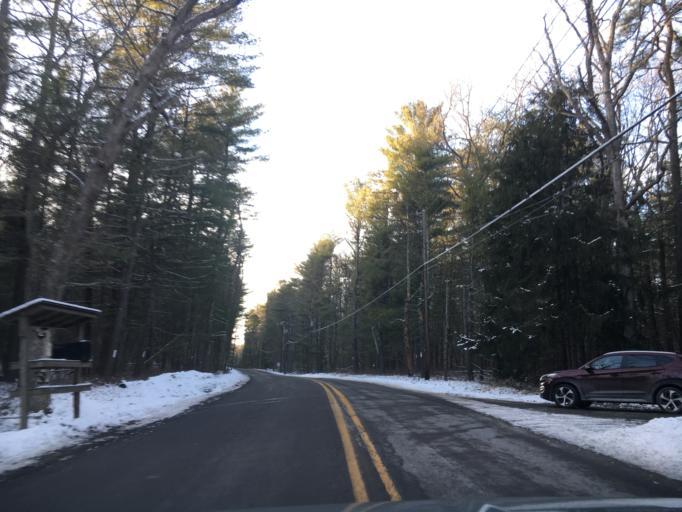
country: US
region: Pennsylvania
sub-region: Pike County
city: Hemlock Farms
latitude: 41.3712
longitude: -75.1053
